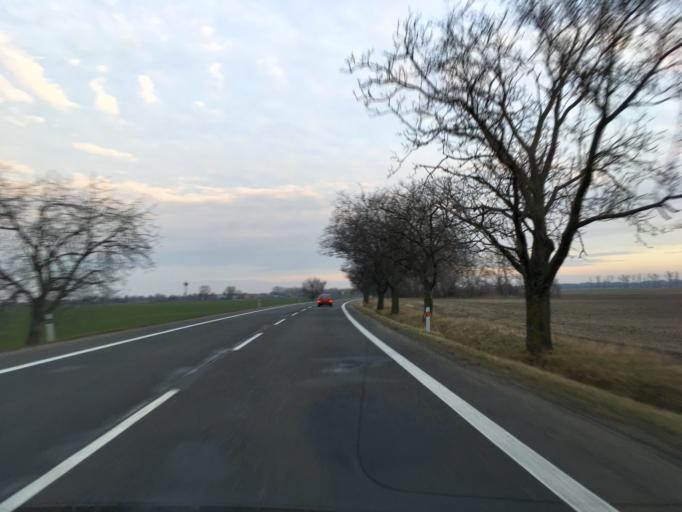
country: HU
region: Komarom-Esztergom
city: Acs
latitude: 47.7746
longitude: 17.9514
